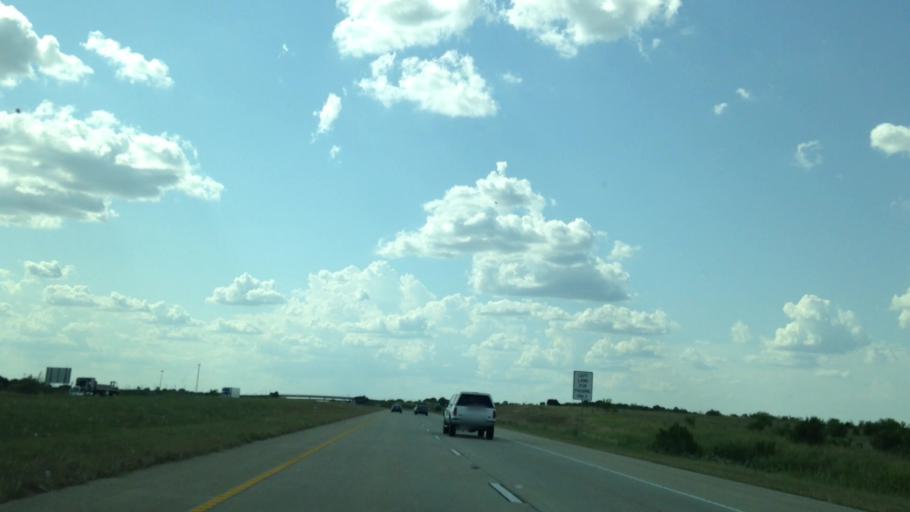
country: US
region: Texas
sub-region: Travis County
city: Onion Creek
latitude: 30.0883
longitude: -97.7448
